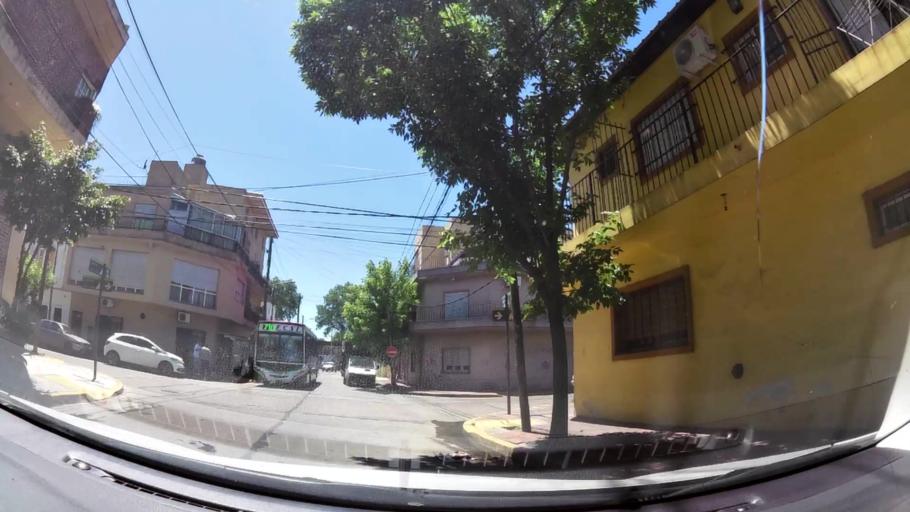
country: AR
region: Buenos Aires
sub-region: Partido de Tigre
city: Tigre
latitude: -34.4513
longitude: -58.5513
